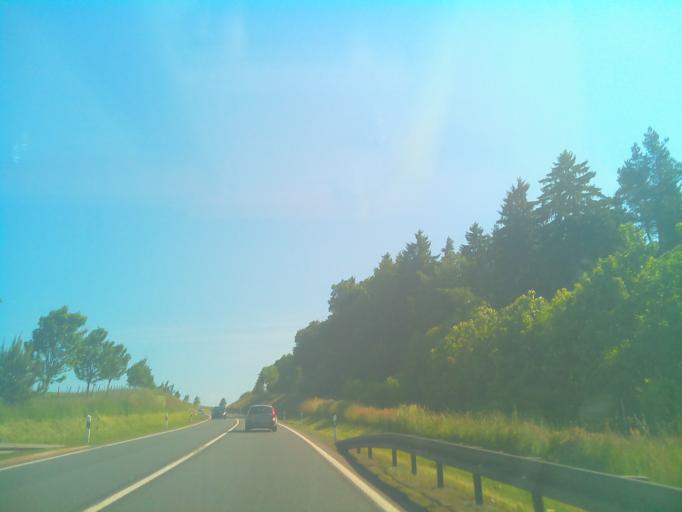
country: DE
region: Thuringia
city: Langewiesen
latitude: 50.7109
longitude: 10.9637
